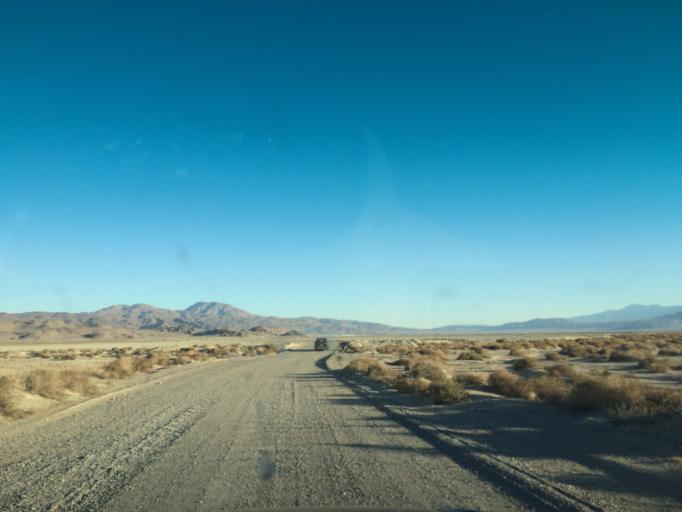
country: US
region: California
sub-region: San Bernardino County
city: Searles Valley
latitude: 35.6510
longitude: -117.3770
